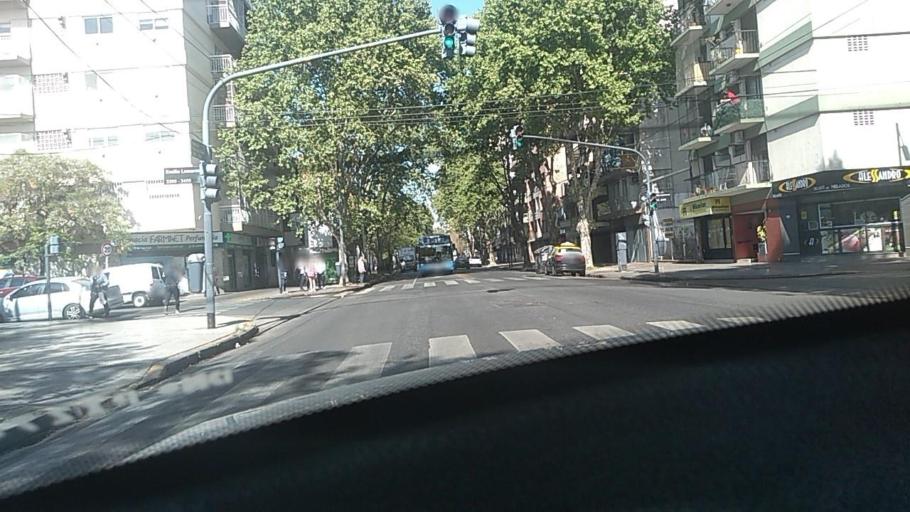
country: AR
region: Buenos Aires F.D.
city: Villa Santa Rita
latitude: -34.6006
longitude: -58.5034
